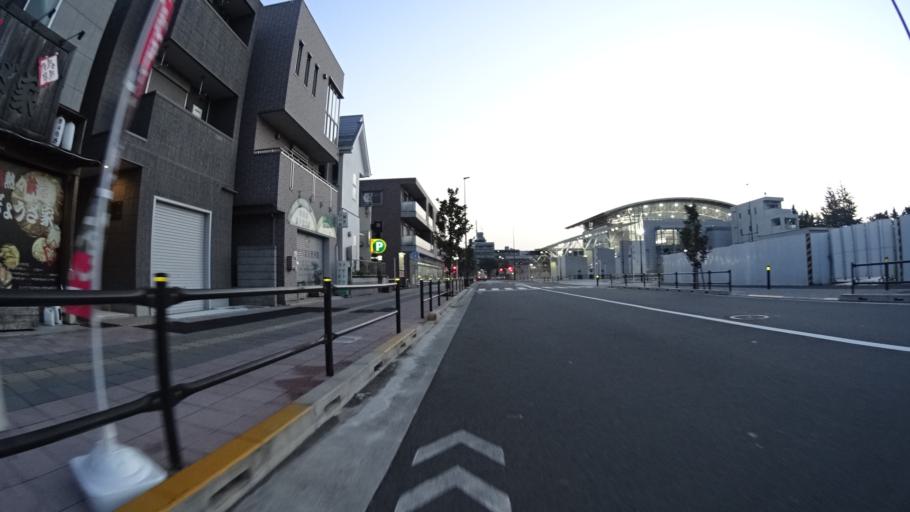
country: JP
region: Tokyo
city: Chofugaoka
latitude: 35.6596
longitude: 139.5221
